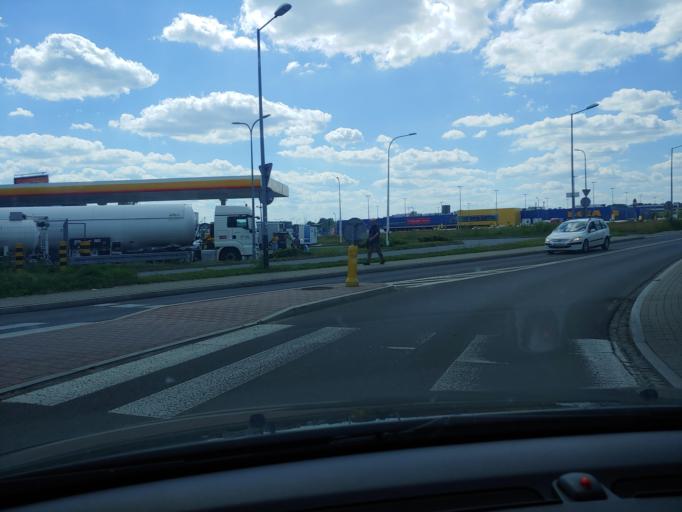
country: PL
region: Lesser Poland Voivodeship
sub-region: Powiat krakowski
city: Zielonki
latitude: 50.0899
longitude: 19.9033
